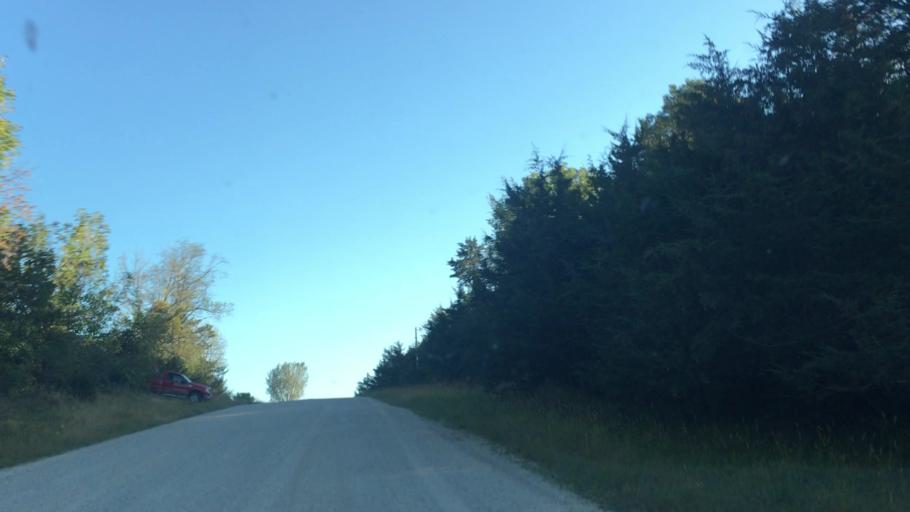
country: US
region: Minnesota
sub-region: Fillmore County
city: Preston
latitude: 43.7777
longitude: -92.0294
